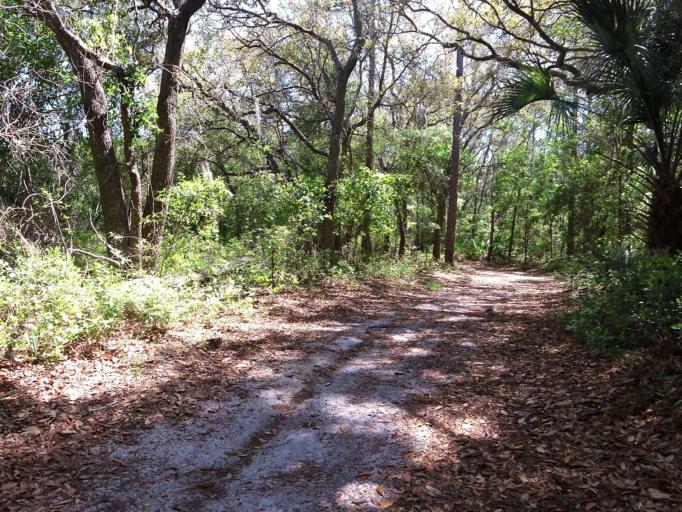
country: US
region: Florida
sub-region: Duval County
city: Atlantic Beach
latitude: 30.4575
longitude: -81.4865
